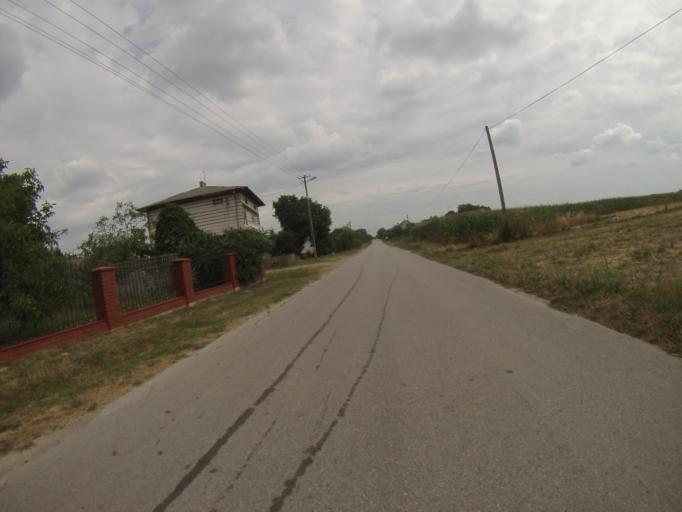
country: PL
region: Swietokrzyskie
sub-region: Powiat kielecki
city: Lagow
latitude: 50.7189
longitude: 21.1192
